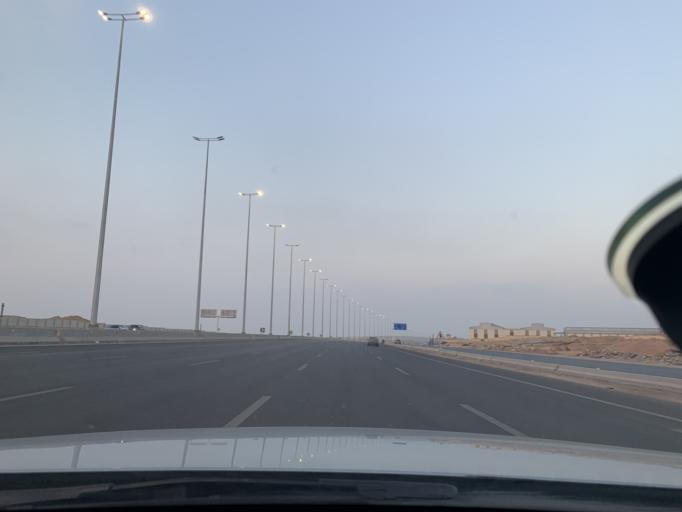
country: EG
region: Muhafazat al Qalyubiyah
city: Al Khankah
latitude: 30.0884
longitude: 31.4612
